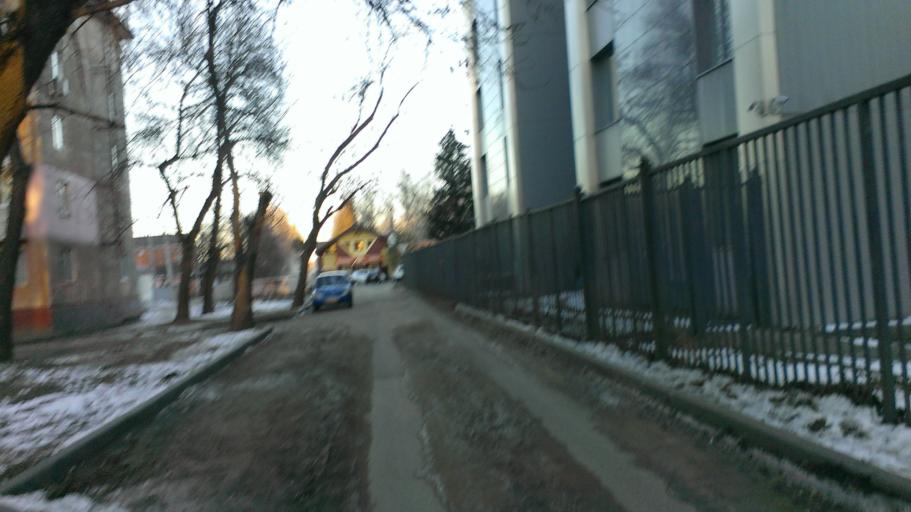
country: RU
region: Tula
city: Tula
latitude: 54.1946
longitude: 37.6905
